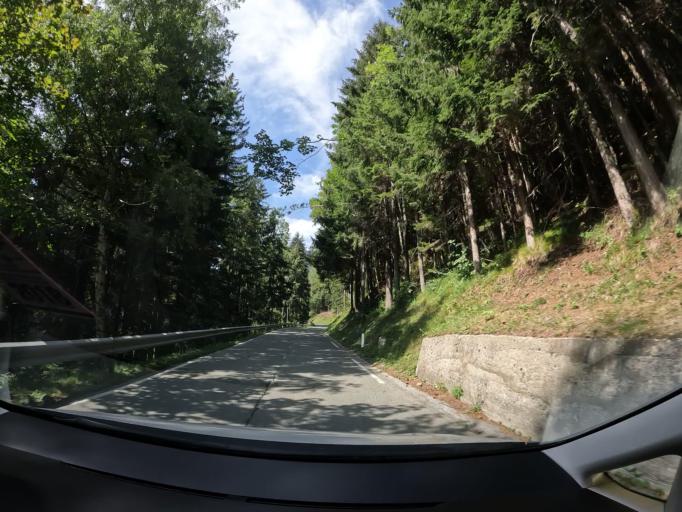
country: AT
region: Carinthia
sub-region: Politischer Bezirk Feldkirchen
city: Glanegg
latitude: 46.7354
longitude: 14.2126
